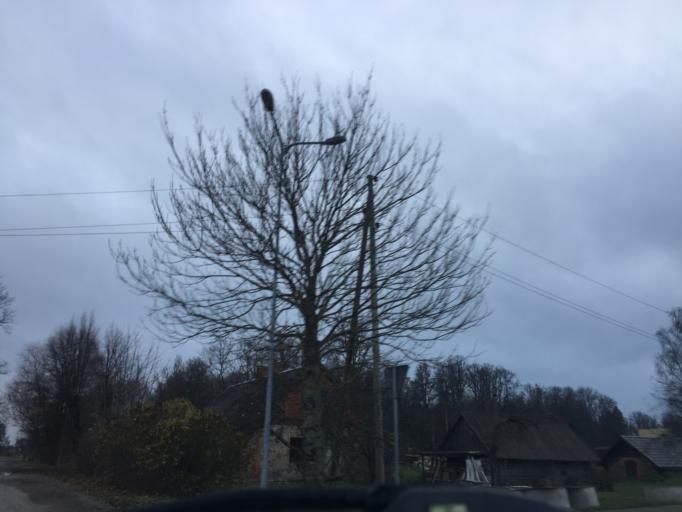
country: LV
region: Aloja
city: Aloja
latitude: 57.6912
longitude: 24.8832
